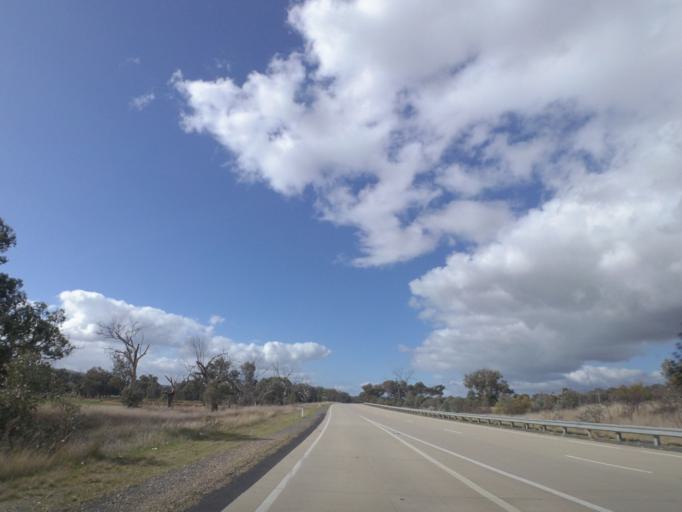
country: AU
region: New South Wales
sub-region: Greater Hume Shire
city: Holbrook
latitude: -35.6790
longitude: 147.3678
